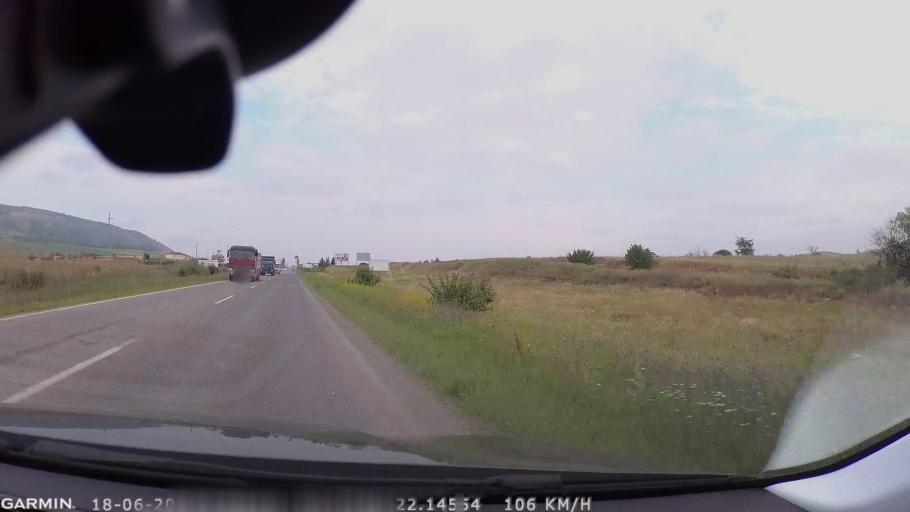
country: MK
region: Stip
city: Shtip
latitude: 41.7717
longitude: 22.1441
